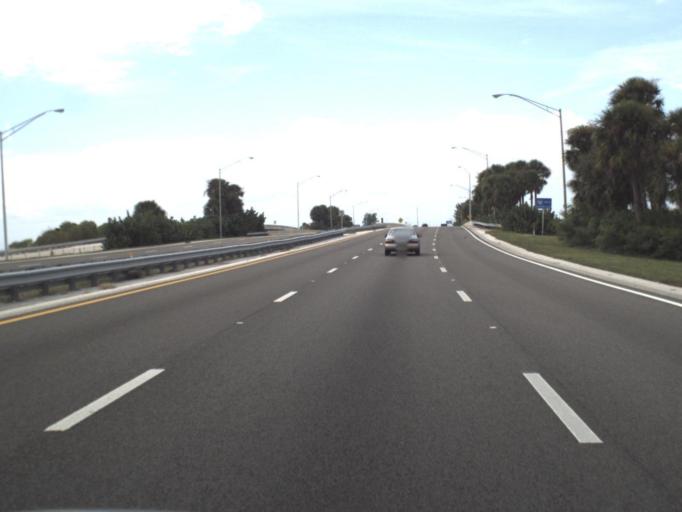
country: US
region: Florida
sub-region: Manatee County
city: Memphis
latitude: 27.5858
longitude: -82.6185
